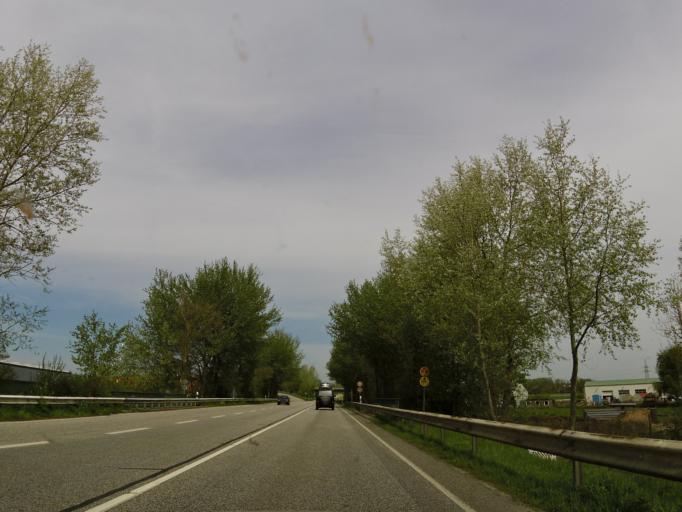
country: DE
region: Schleswig-Holstein
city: Tonning
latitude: 54.3214
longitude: 8.9553
